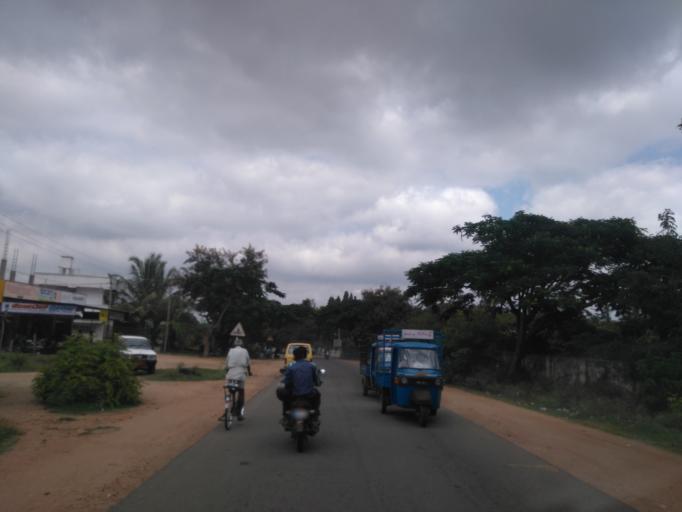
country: IN
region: Karnataka
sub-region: Mysore
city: Mysore
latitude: 12.2899
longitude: 76.7123
